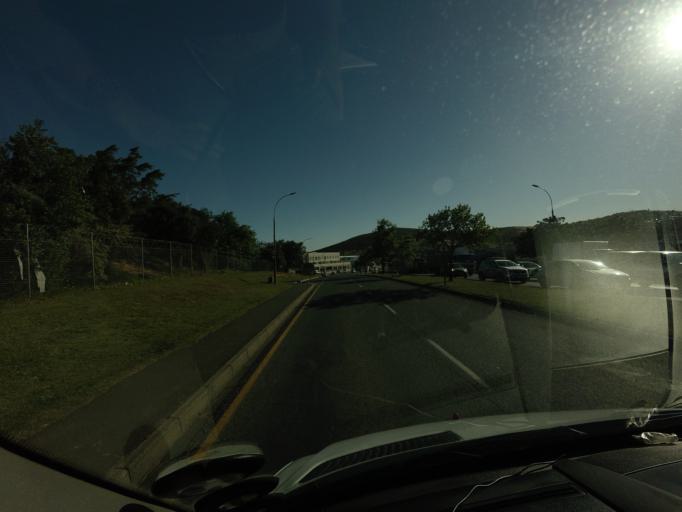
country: ZA
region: Western Cape
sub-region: Cape Winelands District Municipality
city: Stellenbosch
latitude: -33.9237
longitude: 18.8570
